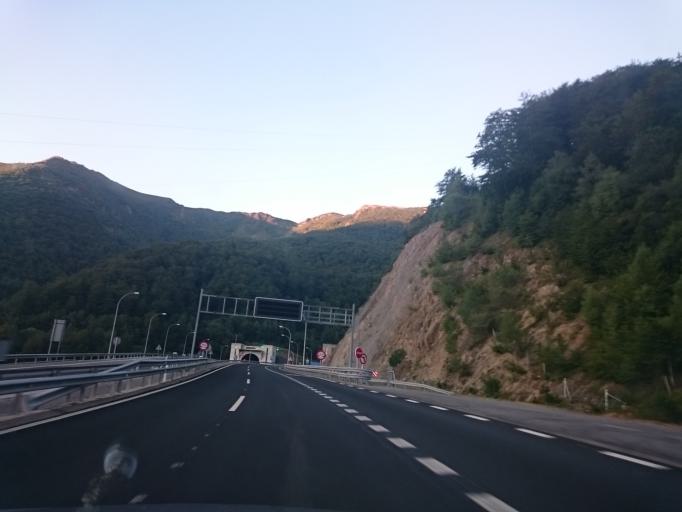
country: ES
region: Castille and Leon
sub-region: Provincia de Leon
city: Sena de Luna
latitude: 42.9812
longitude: -5.8312
